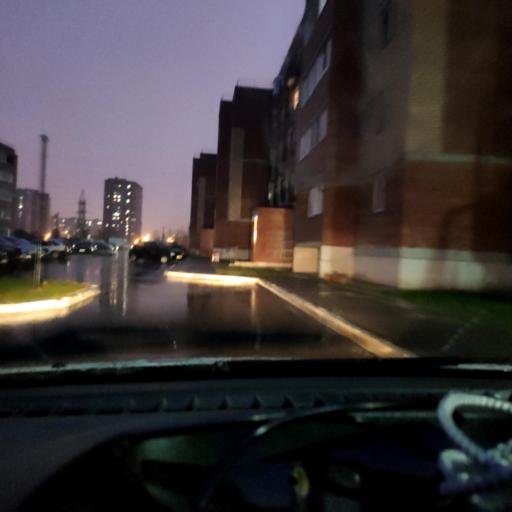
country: RU
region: Samara
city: Tol'yatti
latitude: 53.5458
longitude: 49.3946
